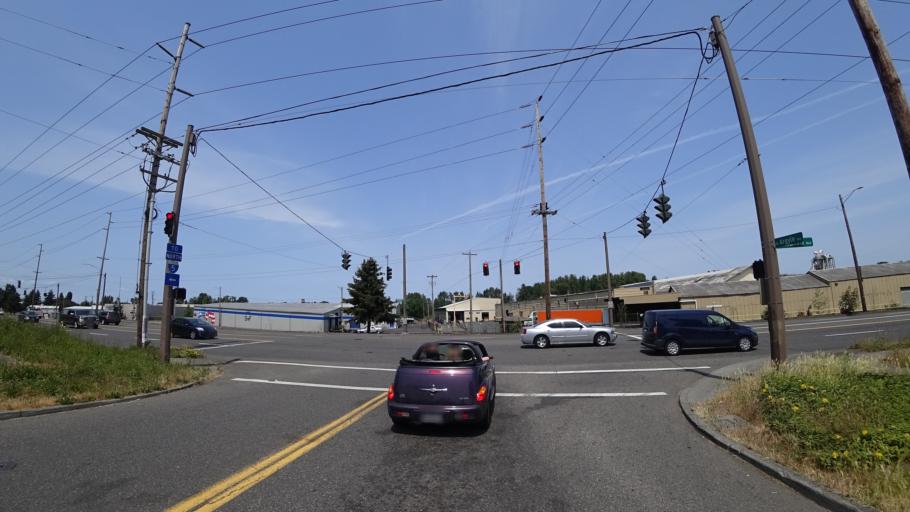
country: US
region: Washington
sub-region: Clark County
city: Vancouver
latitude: 45.5867
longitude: -122.6923
